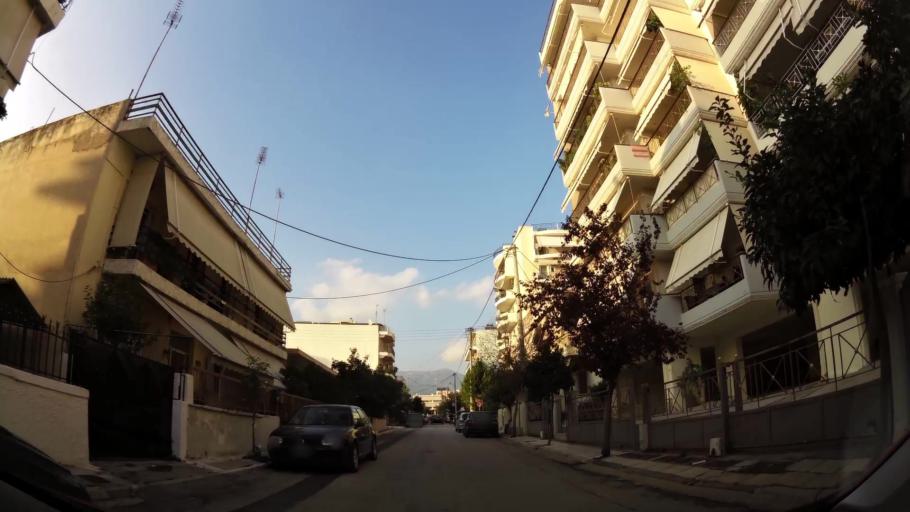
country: GR
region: Attica
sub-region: Nomarchia Anatolikis Attikis
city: Acharnes
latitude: 38.0886
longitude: 23.7346
